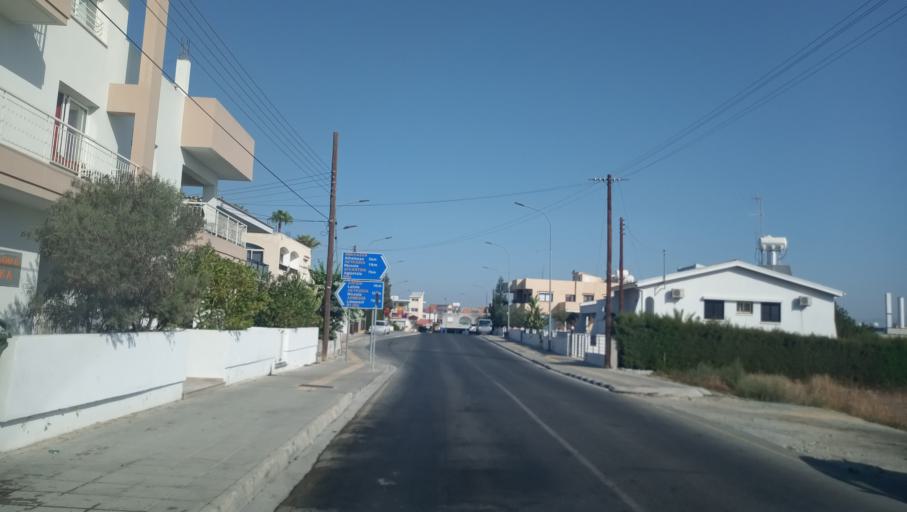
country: CY
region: Lefkosia
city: Geri
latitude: 35.1040
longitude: 33.4144
